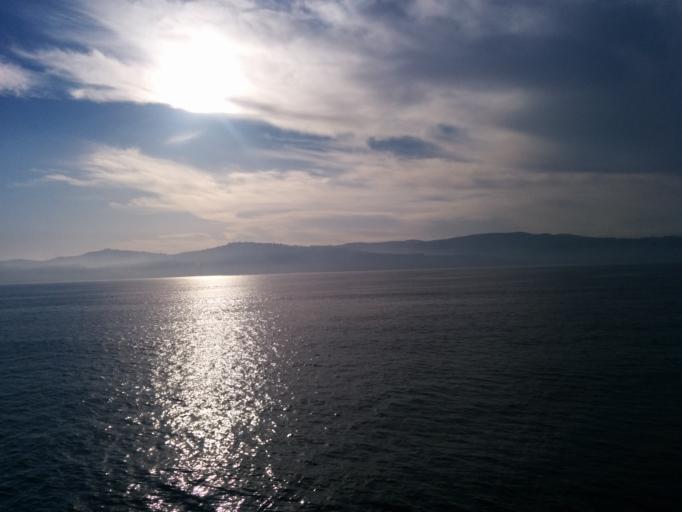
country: MA
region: Tanger-Tetouan
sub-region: Tanger-Assilah
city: Tangier
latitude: 35.8050
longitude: -5.7841
